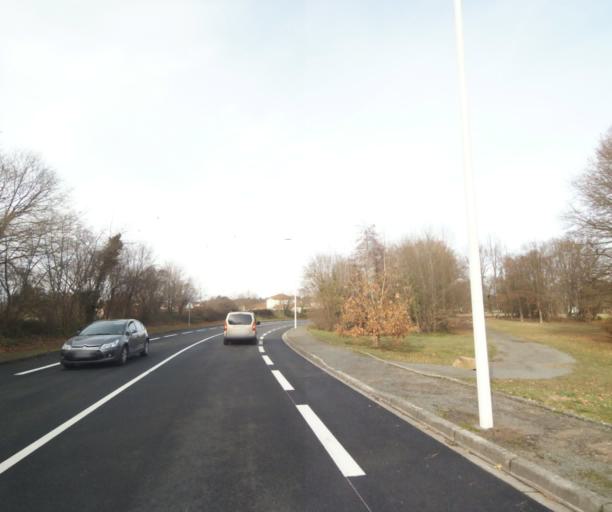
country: FR
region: Rhone-Alpes
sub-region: Departement de la Loire
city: Riorges
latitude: 46.0283
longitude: 4.0479
